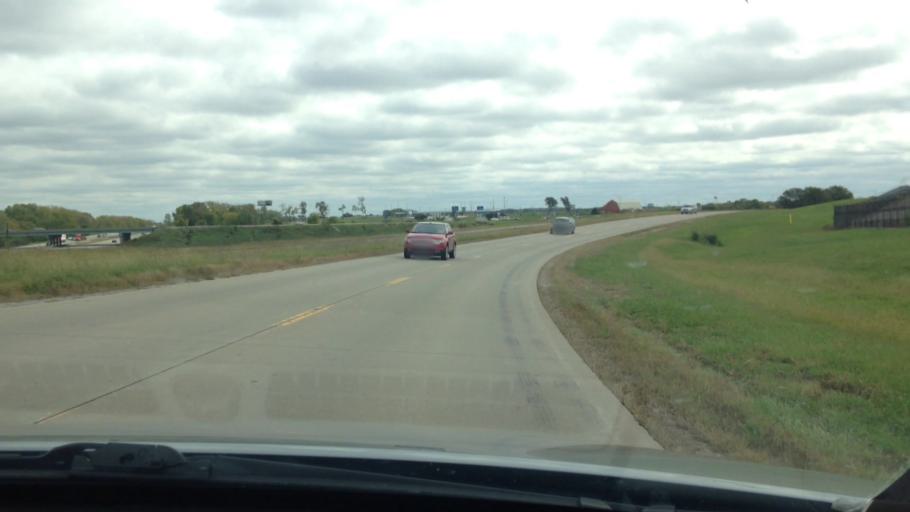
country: US
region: Missouri
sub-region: Platte County
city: Platte City
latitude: 39.3304
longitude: -94.7164
